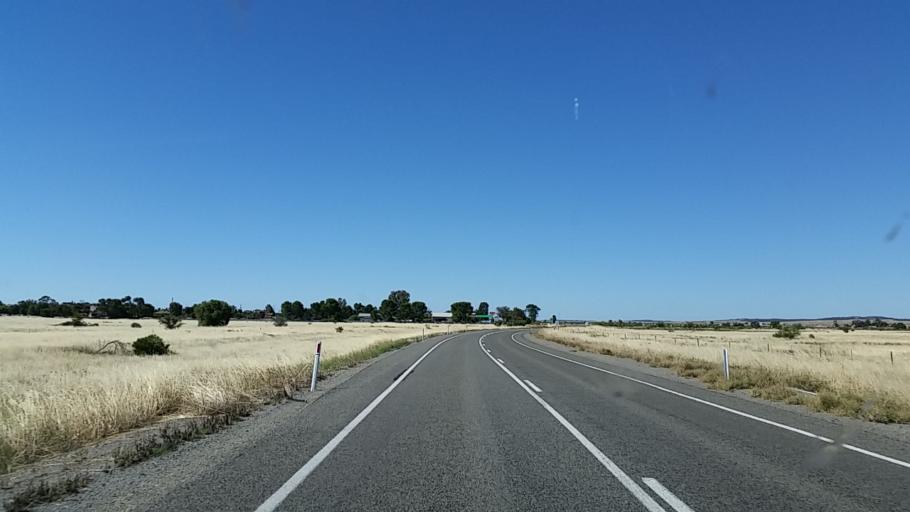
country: AU
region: South Australia
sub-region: Peterborough
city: Peterborough
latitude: -33.1571
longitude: 138.9198
